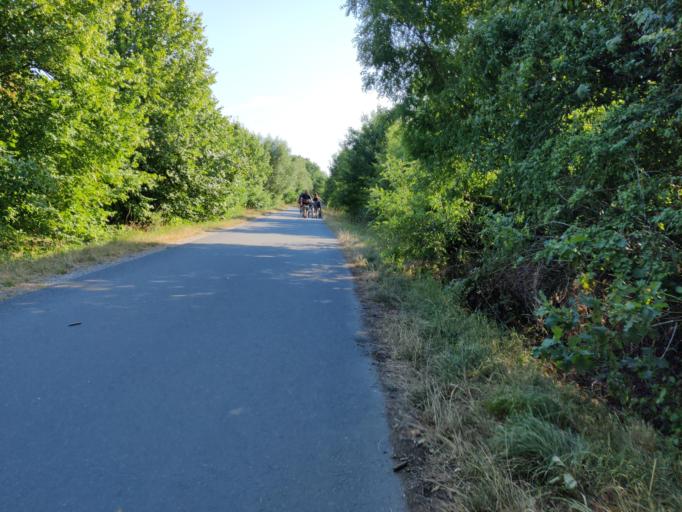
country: DE
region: Saxony
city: Markkleeberg
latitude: 51.2853
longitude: 12.3357
